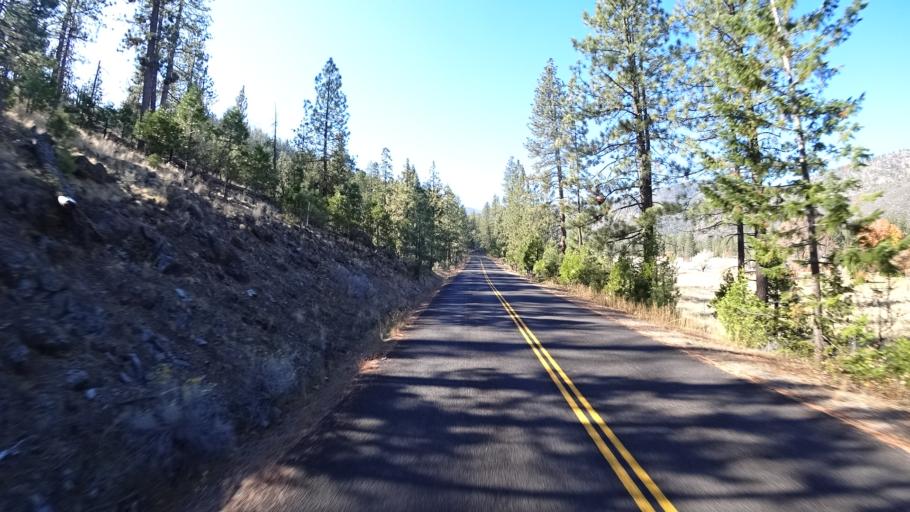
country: US
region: California
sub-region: Siskiyou County
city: Weed
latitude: 41.4329
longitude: -122.4819
